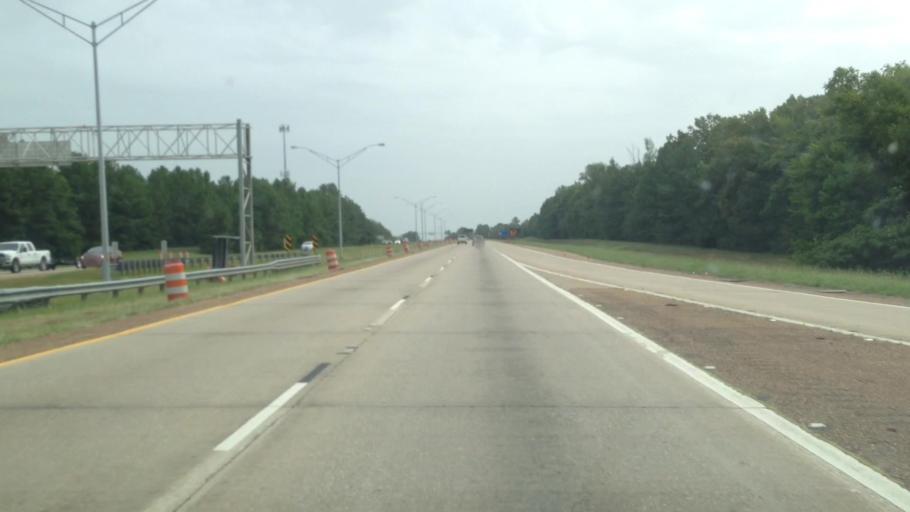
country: US
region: Louisiana
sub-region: Caddo Parish
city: Shreveport
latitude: 32.4878
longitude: -93.8264
